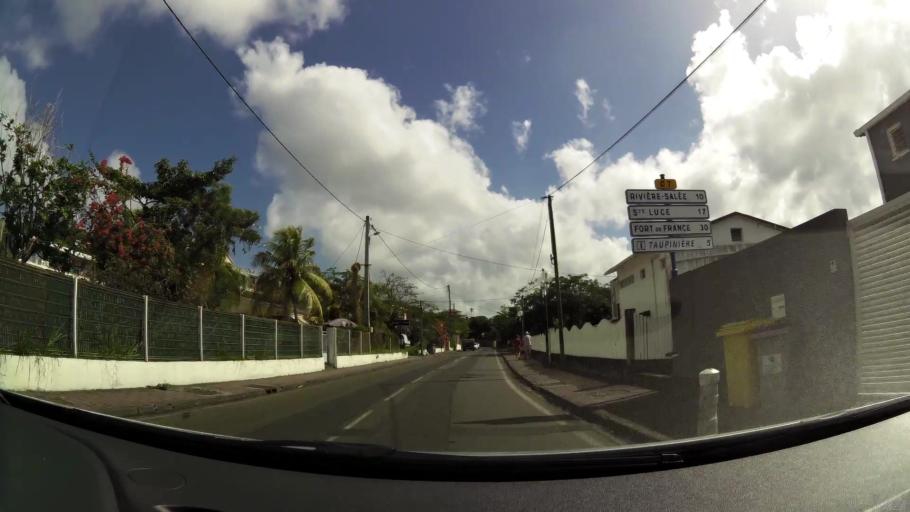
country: MQ
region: Martinique
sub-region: Martinique
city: Les Trois-Ilets
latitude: 14.4810
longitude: -61.0212
